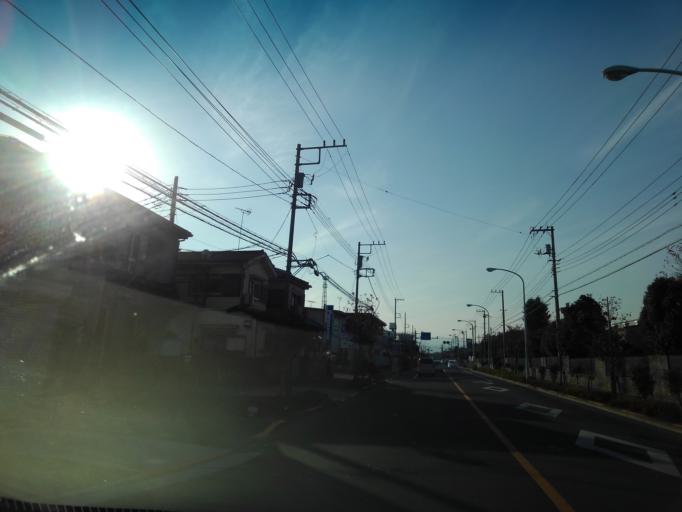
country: JP
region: Tokyo
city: Fussa
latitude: 35.7931
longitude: 139.3466
